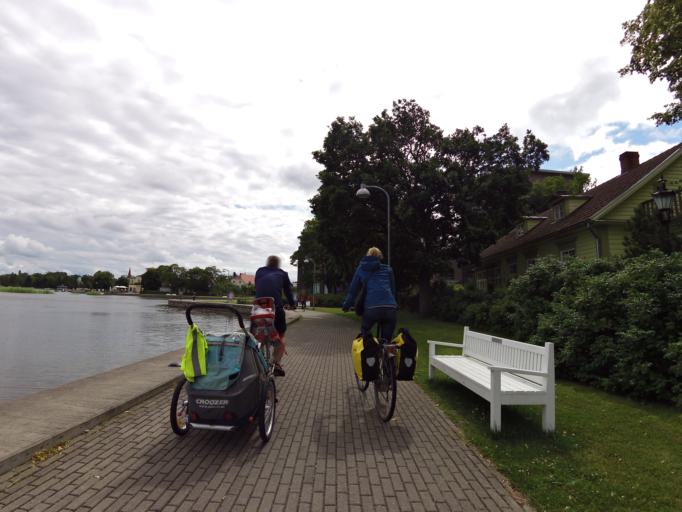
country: EE
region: Laeaene
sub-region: Haapsalu linn
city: Haapsalu
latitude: 58.9530
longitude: 23.5324
